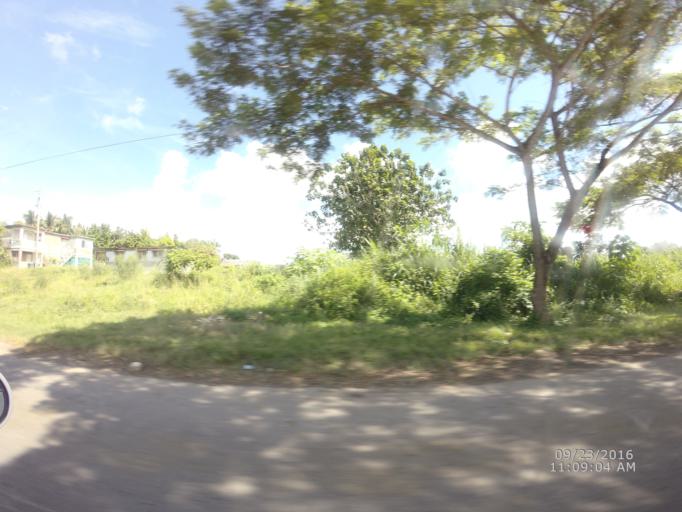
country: CU
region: La Habana
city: Arroyo Naranjo
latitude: 23.0164
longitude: -82.2394
